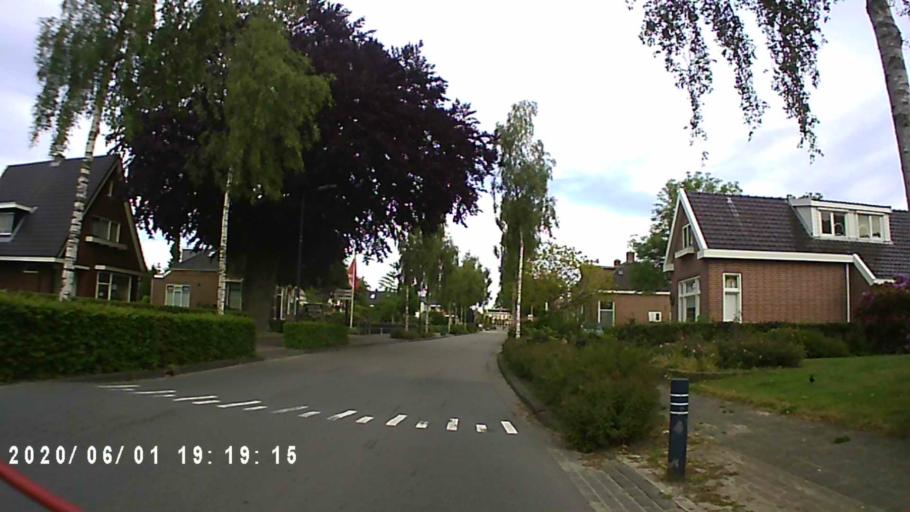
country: NL
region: Friesland
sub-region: Gemeente Achtkarspelen
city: Drogeham
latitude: 53.2039
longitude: 6.1089
